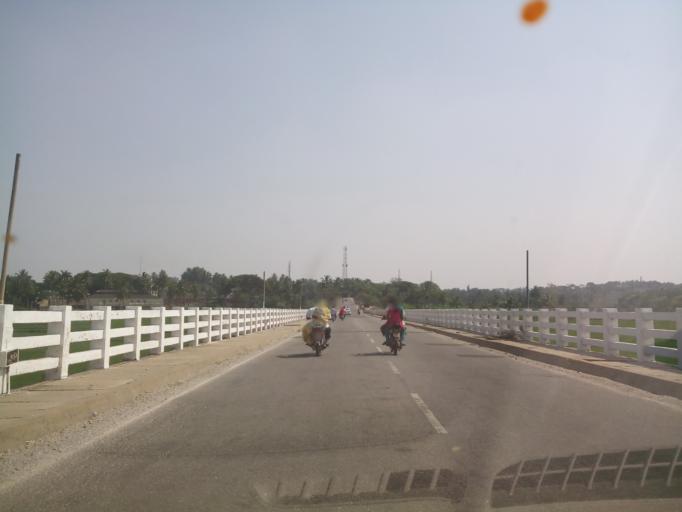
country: IN
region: Karnataka
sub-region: Mandya
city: Shrirangapattana
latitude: 12.4226
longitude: 76.5812
